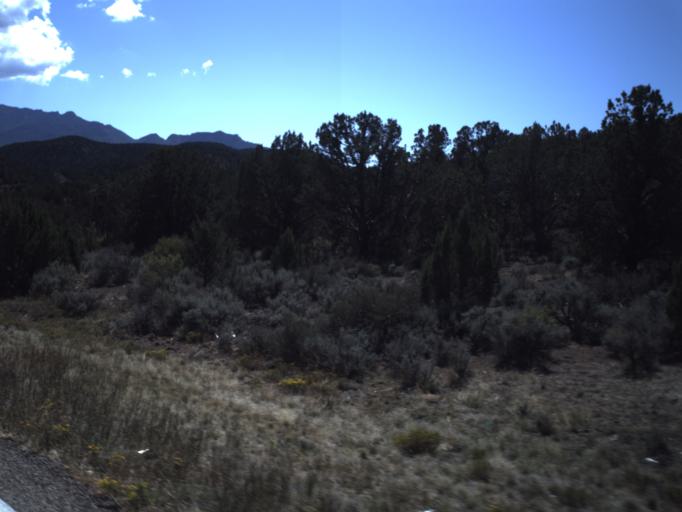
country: US
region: Utah
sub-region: Washington County
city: Enterprise
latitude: 37.4564
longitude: -113.6257
